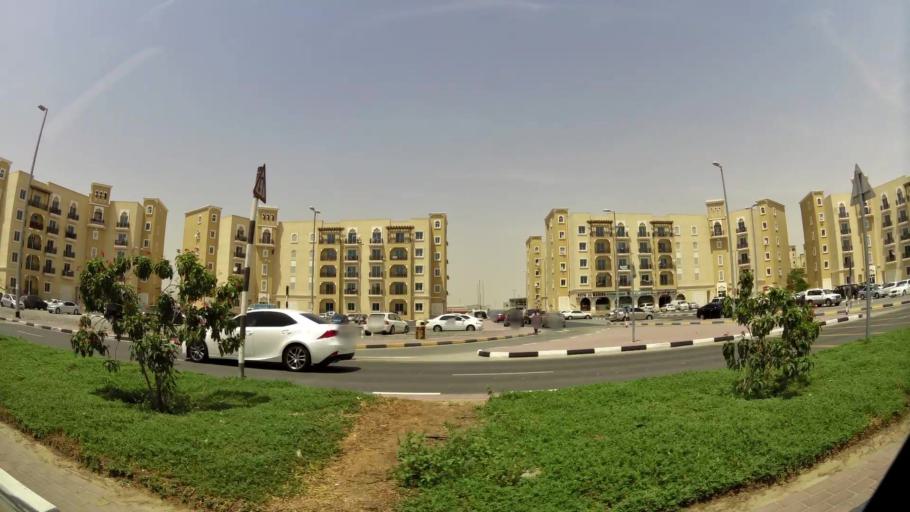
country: AE
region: Ash Shariqah
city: Sharjah
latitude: 25.1630
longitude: 55.4200
